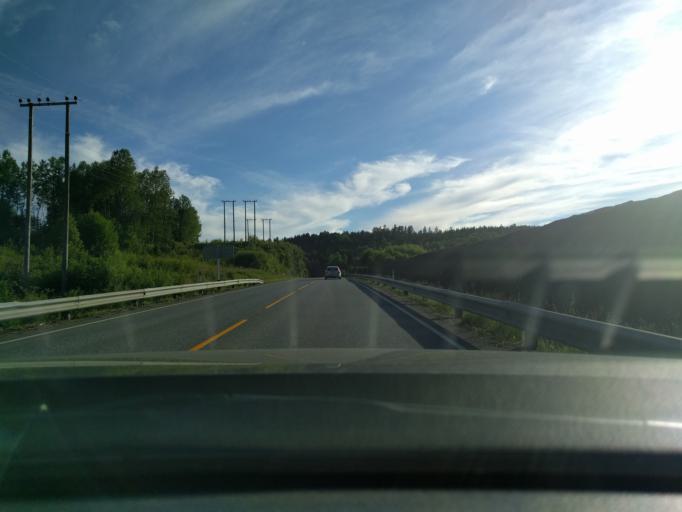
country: NO
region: Vestfold
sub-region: Hof
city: Hof
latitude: 59.5114
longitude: 10.0896
